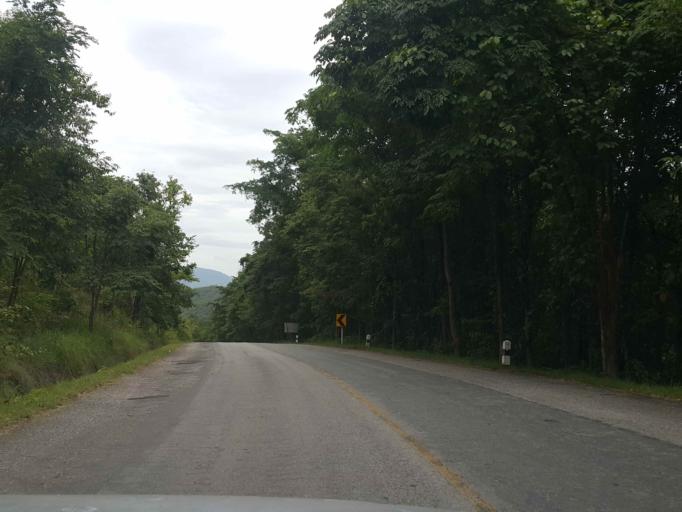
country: TH
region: Lampang
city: Thoen
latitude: 17.6230
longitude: 99.3136
